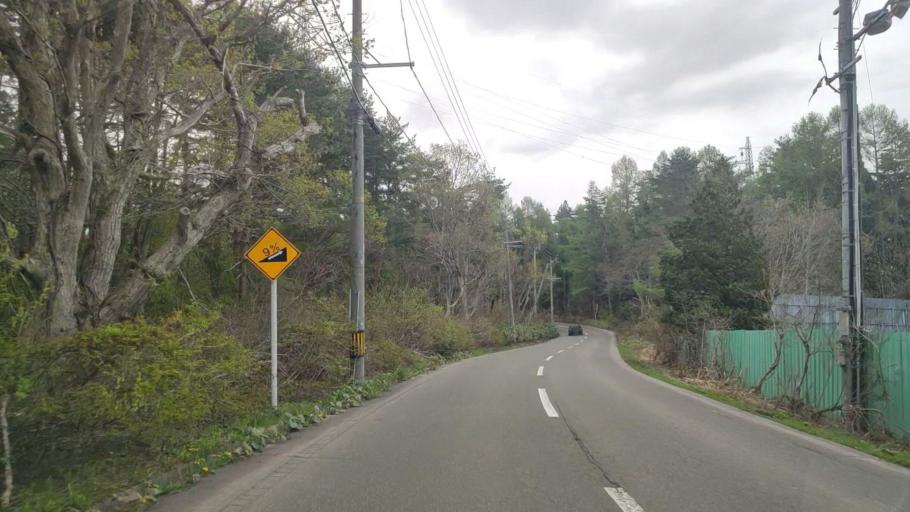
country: JP
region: Aomori
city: Aomori Shi
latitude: 40.7478
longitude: 140.8209
